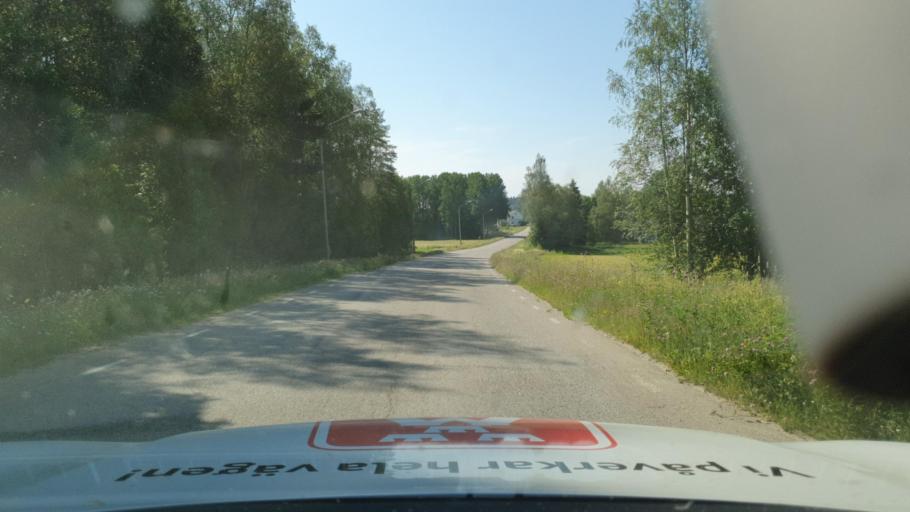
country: SE
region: Vaesterbotten
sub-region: Skelleftea Kommun
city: Burea
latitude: 64.4078
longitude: 21.2915
